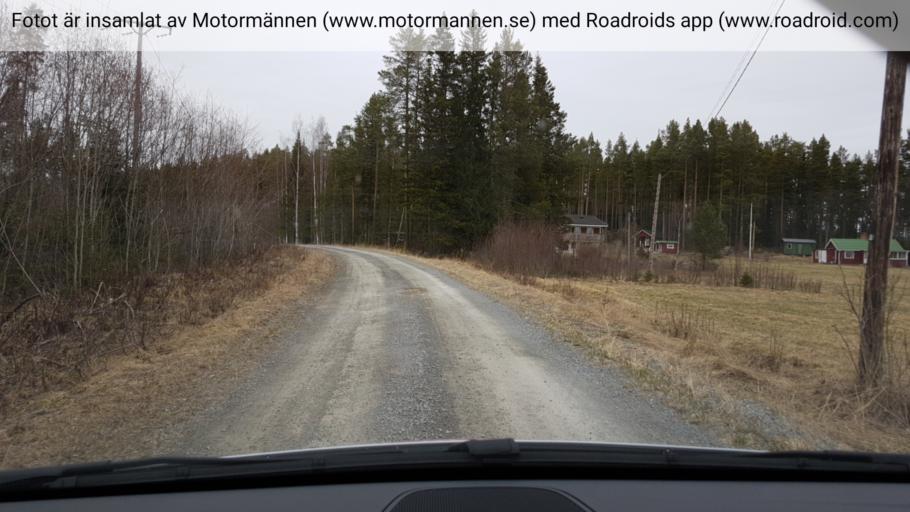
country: SE
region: Jaemtland
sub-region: Bergs Kommun
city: Hoverberg
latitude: 62.8388
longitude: 14.6263
